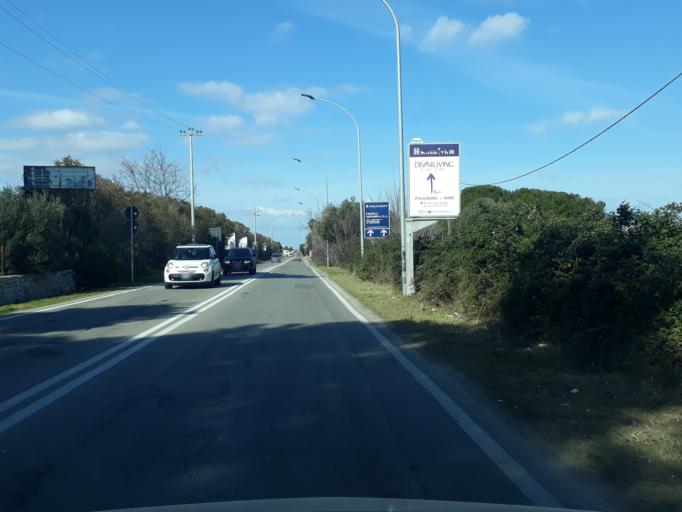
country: IT
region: Apulia
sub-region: Provincia di Bari
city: Monopoli
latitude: 40.9630
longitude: 17.2789
